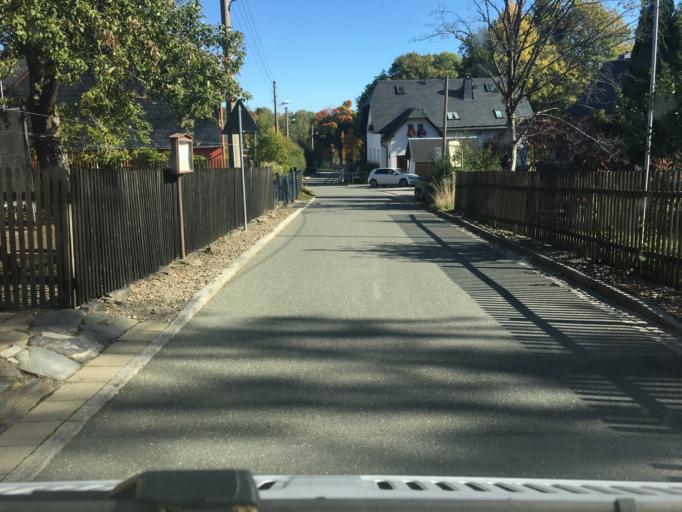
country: DE
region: Saxony
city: Schneeberg
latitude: 50.6048
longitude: 12.6197
